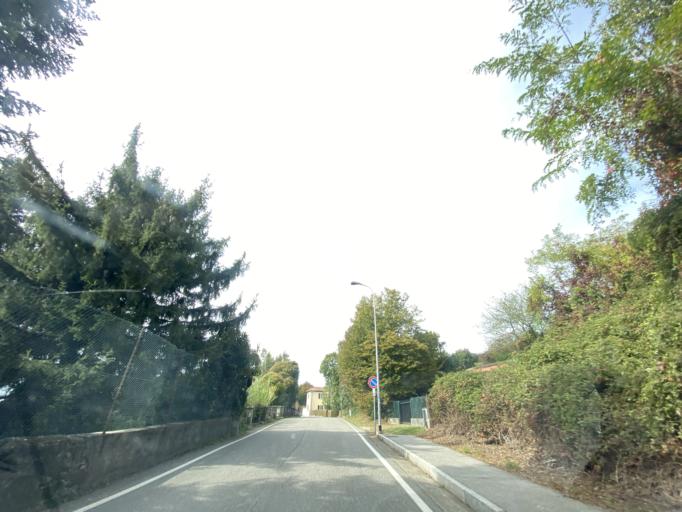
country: IT
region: Lombardy
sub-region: Provincia di Lecco
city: Montevecchia
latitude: 45.7087
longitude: 9.3679
